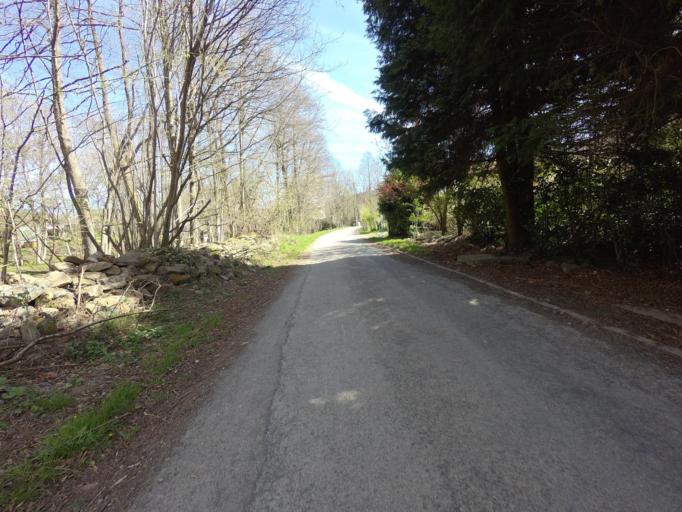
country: BE
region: Wallonia
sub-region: Province de Liege
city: Stavelot
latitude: 50.4259
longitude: 5.8860
